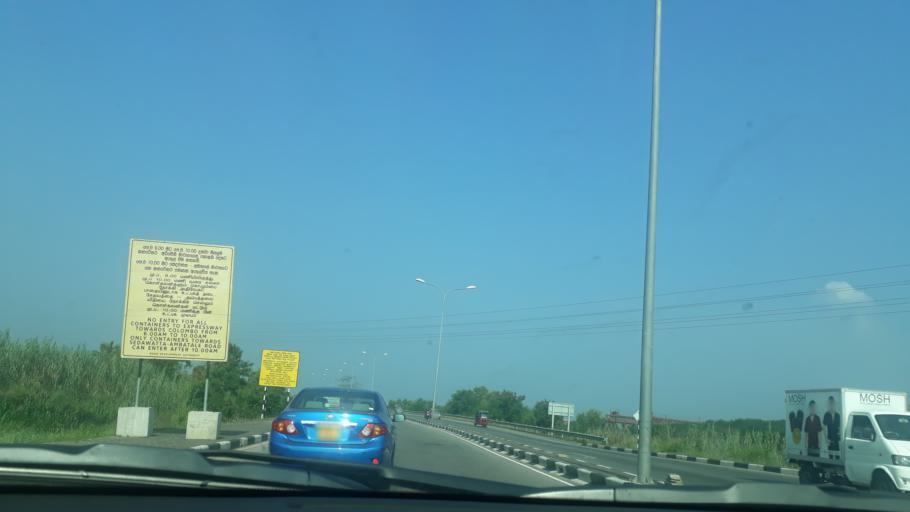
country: LK
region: Western
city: Wattala
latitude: 6.9681
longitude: 79.9010
